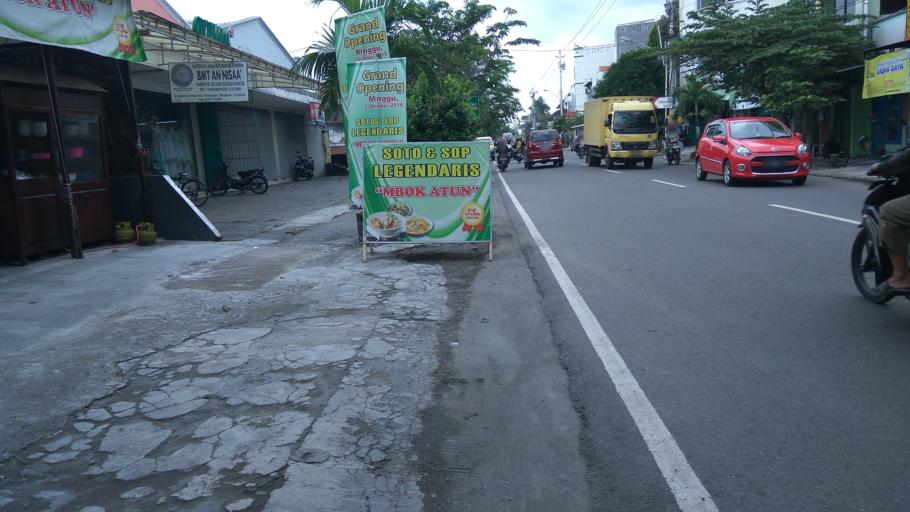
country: ID
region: Central Java
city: Surakarta
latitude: -7.5493
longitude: 110.8214
